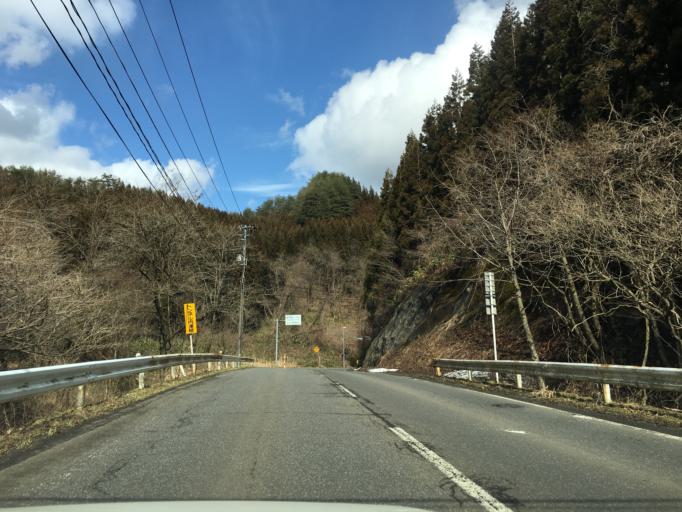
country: JP
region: Akita
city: Odate
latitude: 40.1906
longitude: 140.5200
